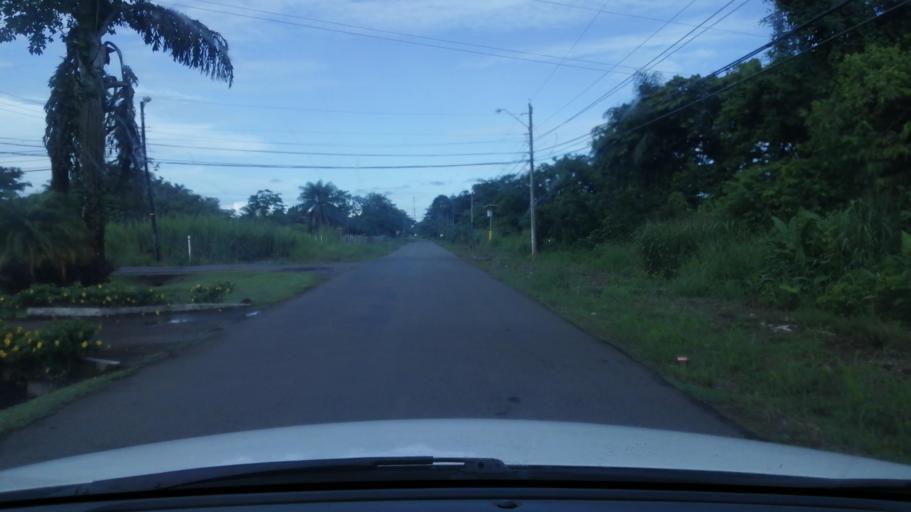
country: PA
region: Chiriqui
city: El Quiteno
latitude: 8.4656
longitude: -82.4149
